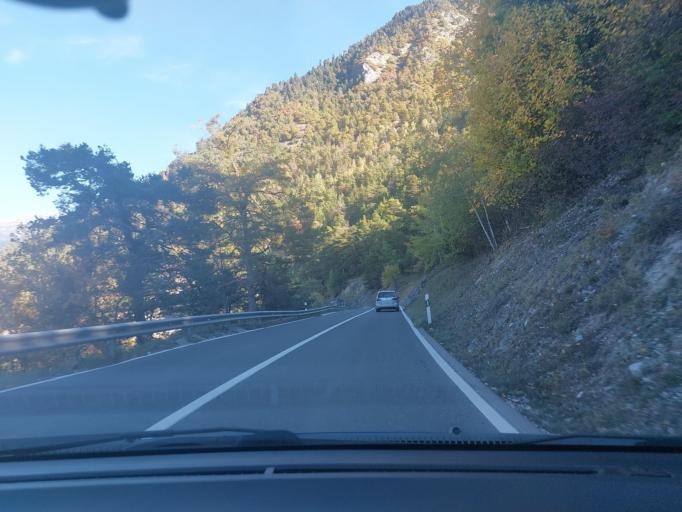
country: CH
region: Valais
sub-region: Sierre District
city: Chippis
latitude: 46.2662
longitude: 7.5559
